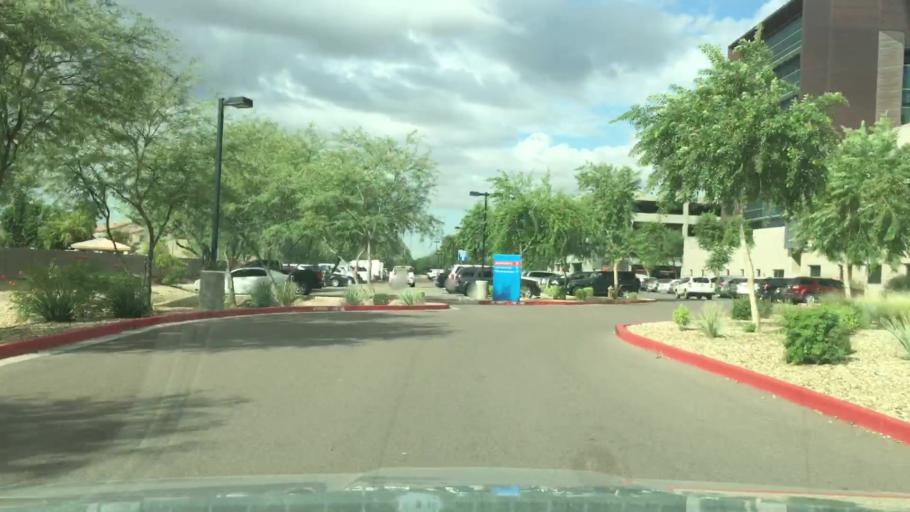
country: US
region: Arizona
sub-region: Maricopa County
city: Tolleson
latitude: 33.4772
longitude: -112.2572
